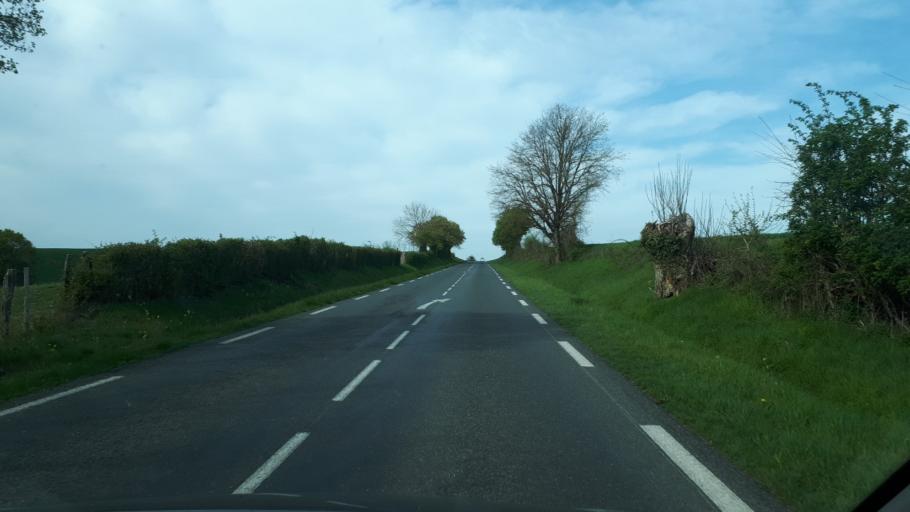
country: FR
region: Centre
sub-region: Departement du Cher
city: Sancerre
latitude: 47.2676
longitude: 2.7245
